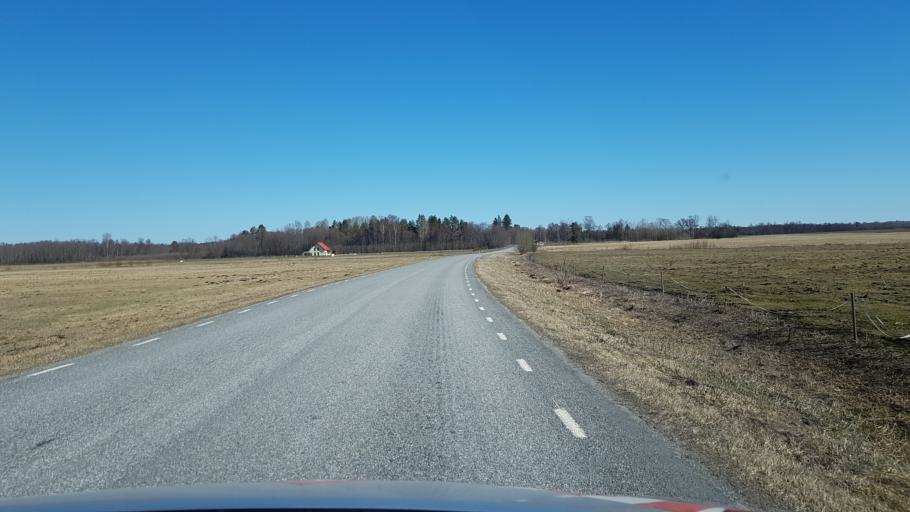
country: EE
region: Laeaene-Virumaa
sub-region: Haljala vald
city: Haljala
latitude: 59.4602
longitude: 26.2338
